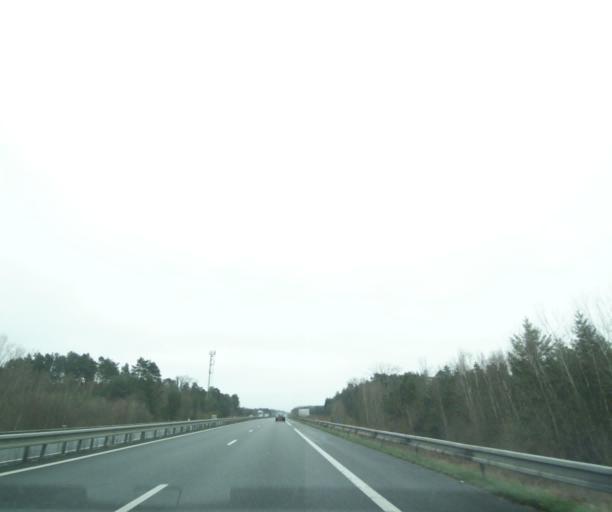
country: FR
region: Centre
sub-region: Departement du Loir-et-Cher
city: Lamotte-Beuvron
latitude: 47.5900
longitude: 1.9885
